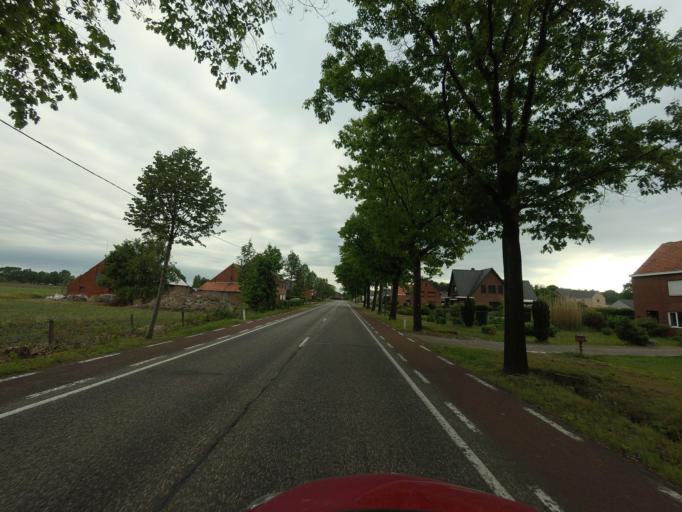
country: BE
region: Flanders
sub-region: Provincie Limburg
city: Leopoldsburg
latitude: 51.1474
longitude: 5.2607
